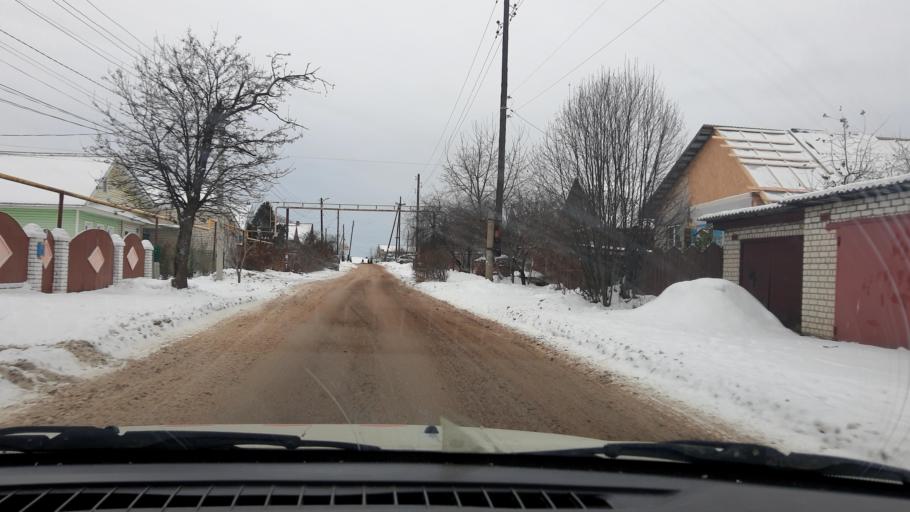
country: RU
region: Nizjnij Novgorod
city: Gorodets
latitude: 56.6593
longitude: 43.4804
